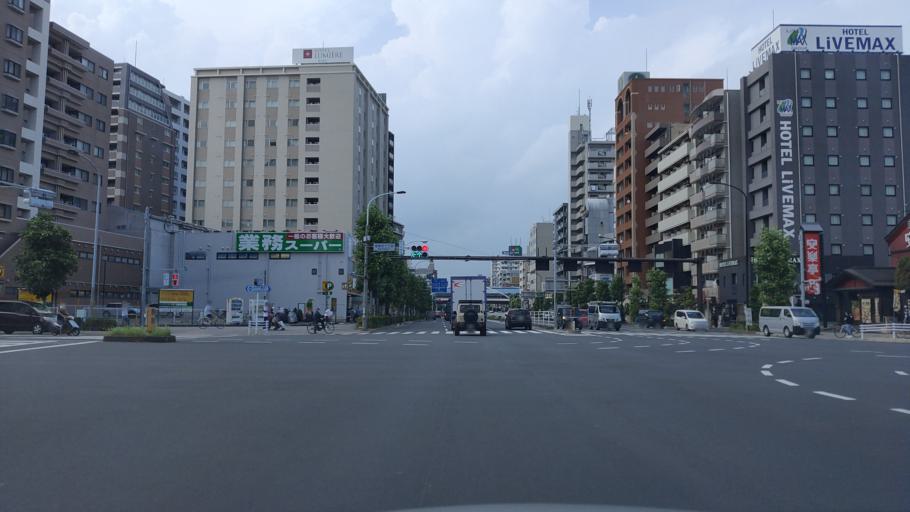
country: JP
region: Tokyo
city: Urayasu
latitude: 35.6600
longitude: 139.8728
